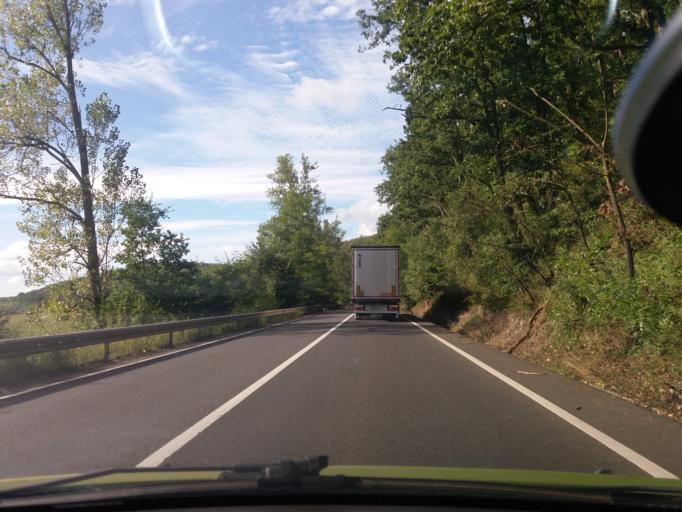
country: RO
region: Arad
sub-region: Comuna Varadia de Mures
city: Varadia de Mures
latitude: 46.0273
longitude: 22.1223
